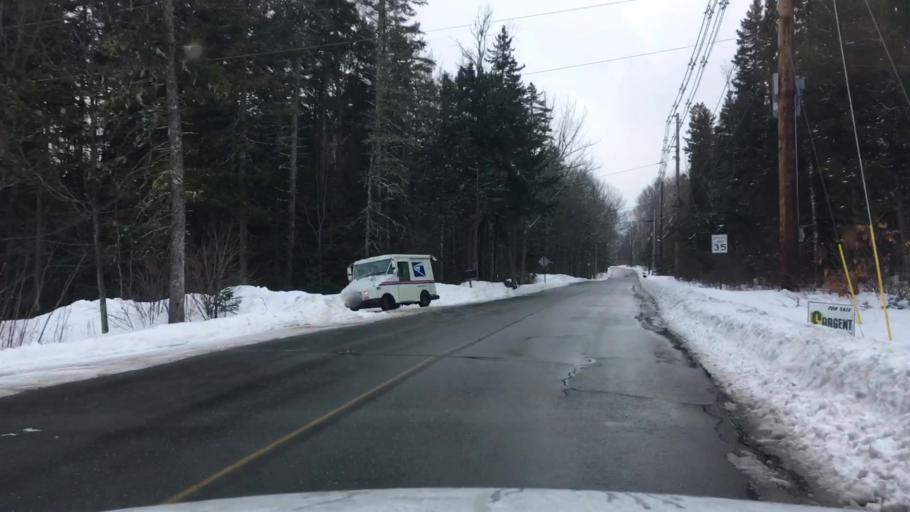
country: US
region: Maine
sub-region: Hancock County
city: Trenton
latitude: 44.4200
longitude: -68.3335
